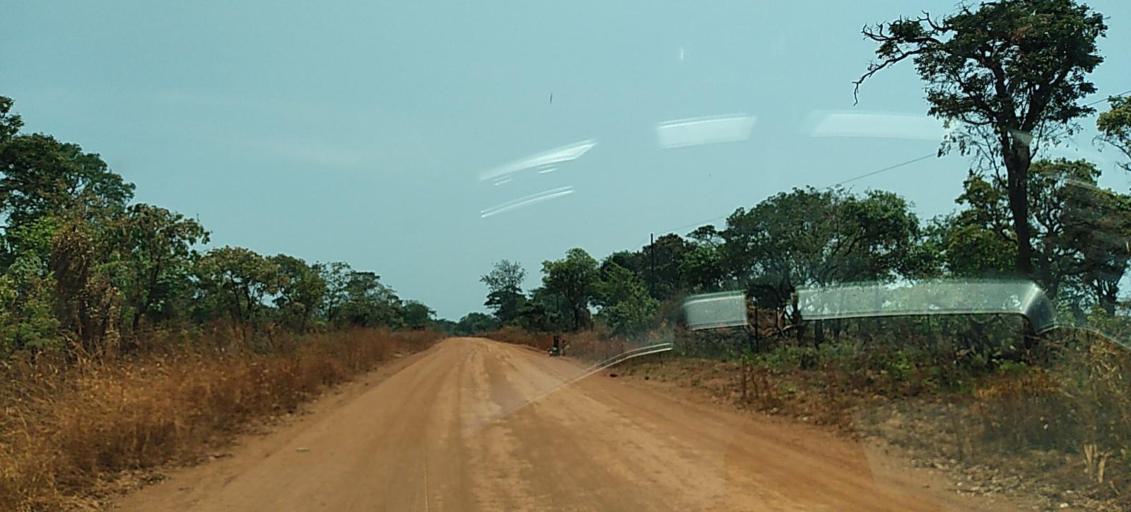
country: CD
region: Katanga
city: Kipushi
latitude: -11.9763
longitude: 26.8928
